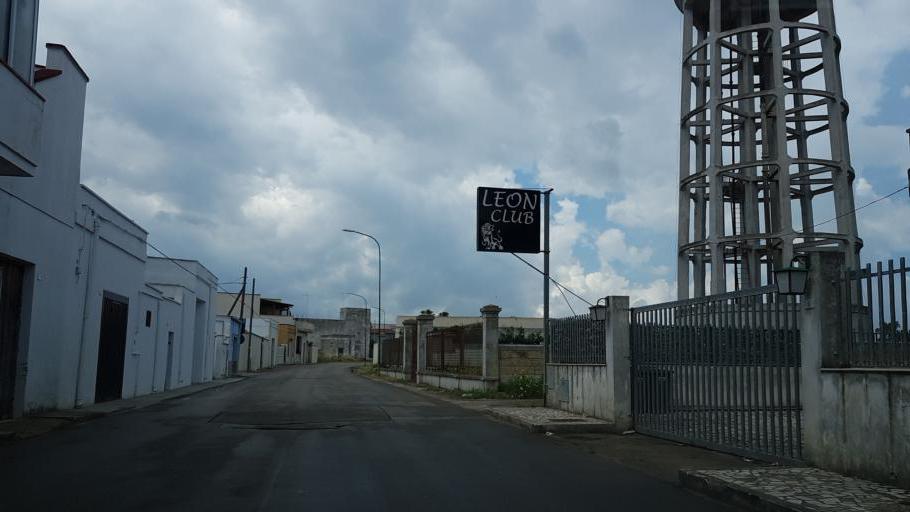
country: IT
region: Apulia
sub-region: Provincia di Brindisi
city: San Donaci
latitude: 40.4510
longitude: 17.9198
